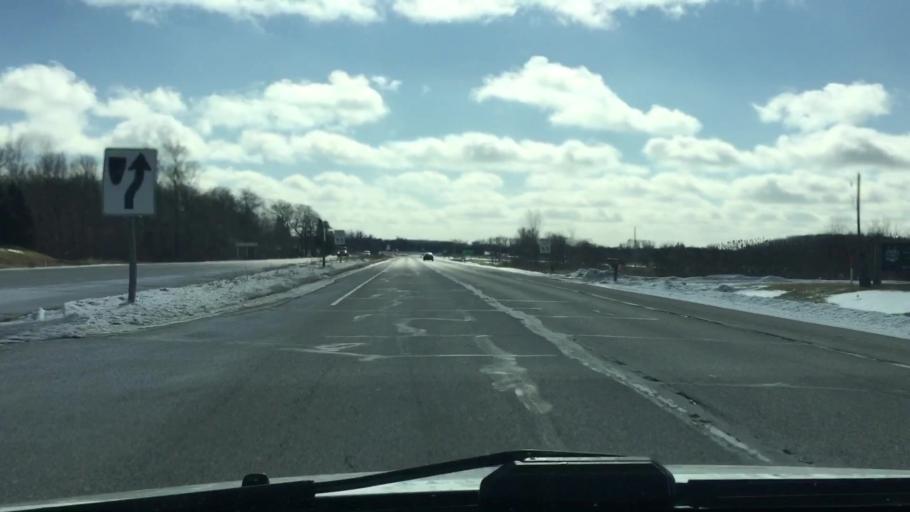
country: US
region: Wisconsin
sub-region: Waukesha County
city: Big Bend
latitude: 42.9336
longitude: -88.2286
